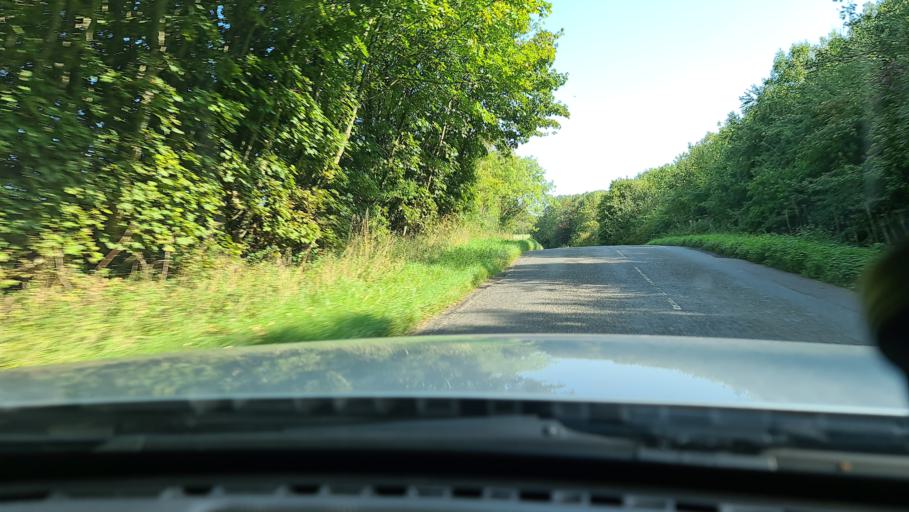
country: GB
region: England
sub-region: Northamptonshire
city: Brackley
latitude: 52.1129
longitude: -1.1958
